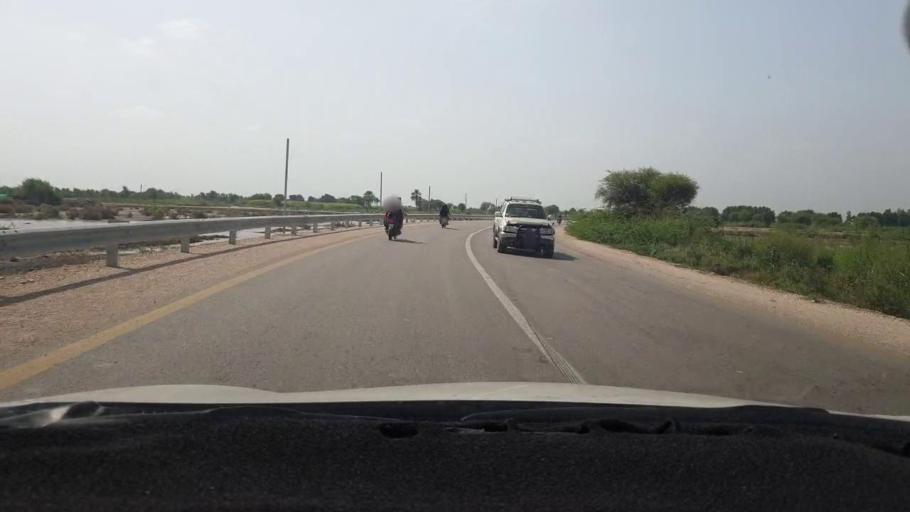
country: PK
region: Sindh
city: Mirpur Khas
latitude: 25.5883
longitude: 69.0757
